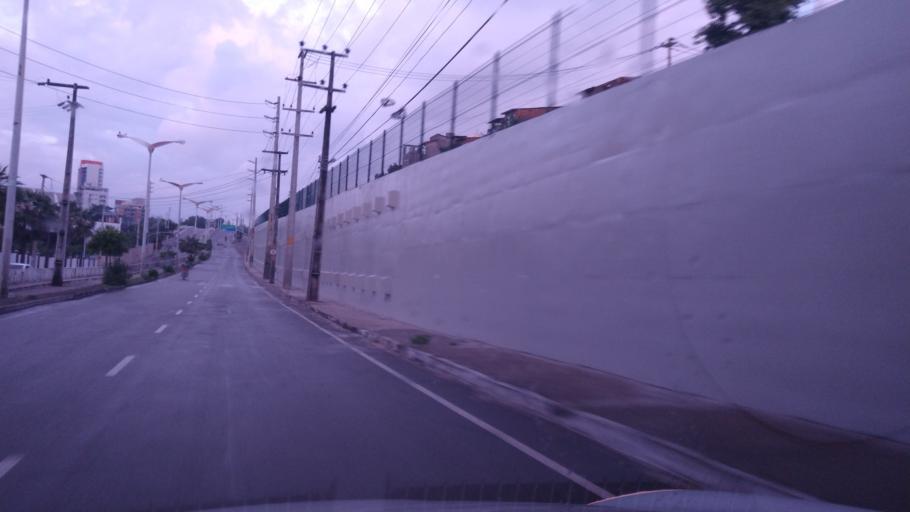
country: BR
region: Ceara
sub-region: Fortaleza
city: Fortaleza
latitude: -3.7459
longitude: -38.4911
